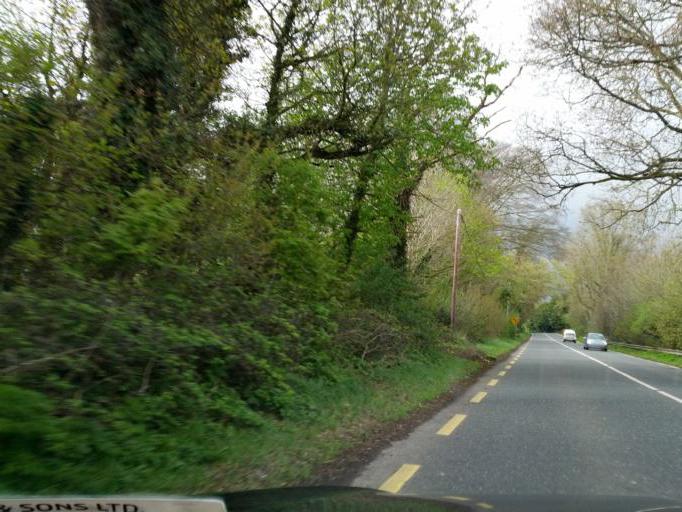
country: IE
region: Leinster
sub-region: An Mhi
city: Dunshaughlin
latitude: 53.5282
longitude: -6.5572
